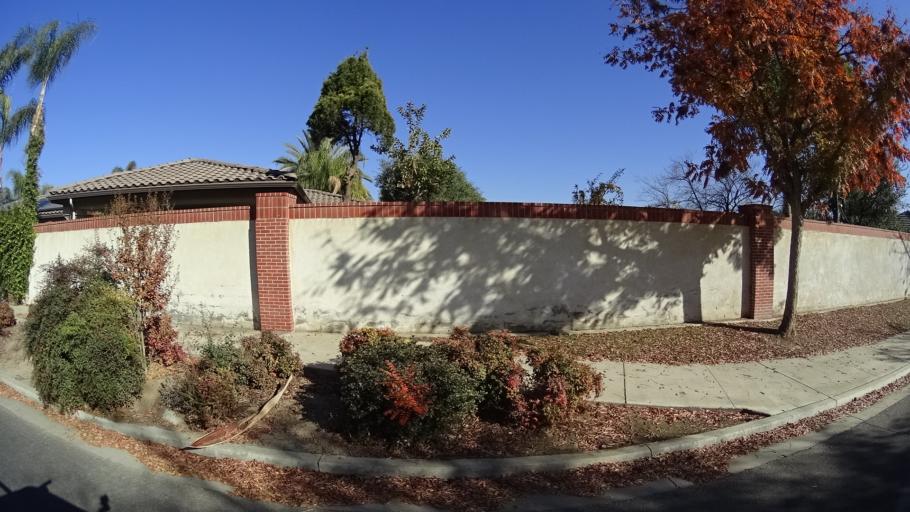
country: US
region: California
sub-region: Kern County
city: Rosedale
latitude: 35.3296
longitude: -119.1420
